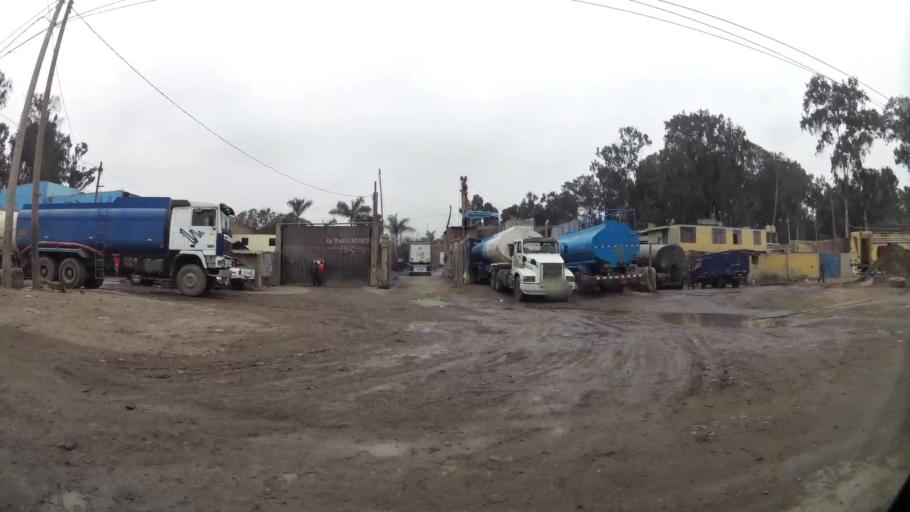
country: PE
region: Lima
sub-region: Lima
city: Surco
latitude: -12.1875
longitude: -76.9729
